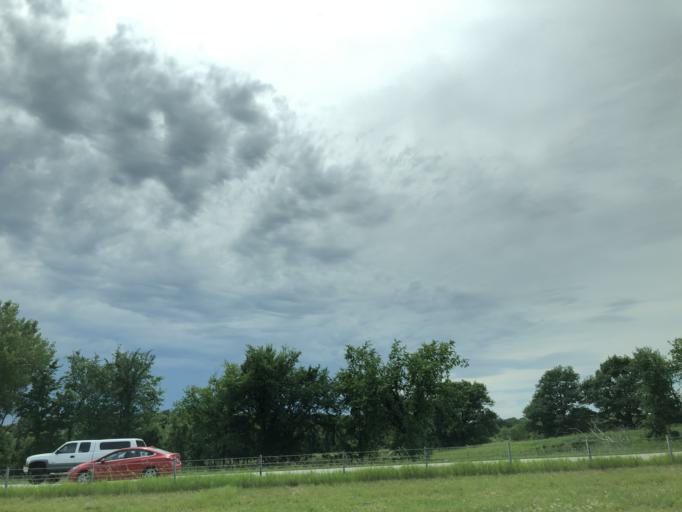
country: US
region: Minnesota
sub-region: Stearns County
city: Collegeville
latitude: 45.5681
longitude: -94.3518
